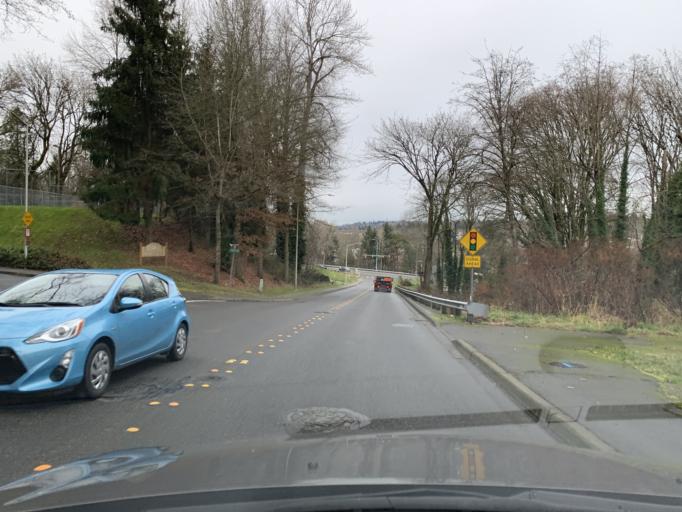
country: US
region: Washington
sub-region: King County
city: Tukwila
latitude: 47.4595
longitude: -122.2678
